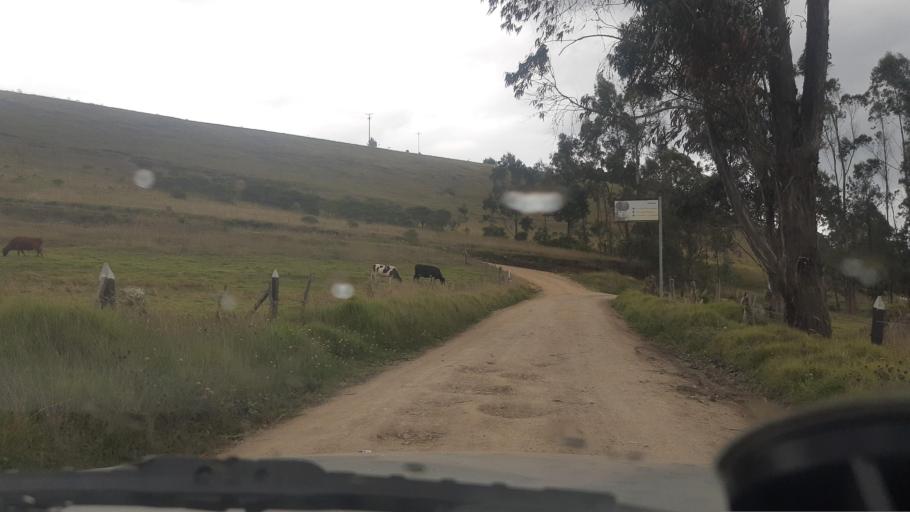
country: CO
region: Cundinamarca
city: Suesca
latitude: 5.1749
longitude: -73.8027
